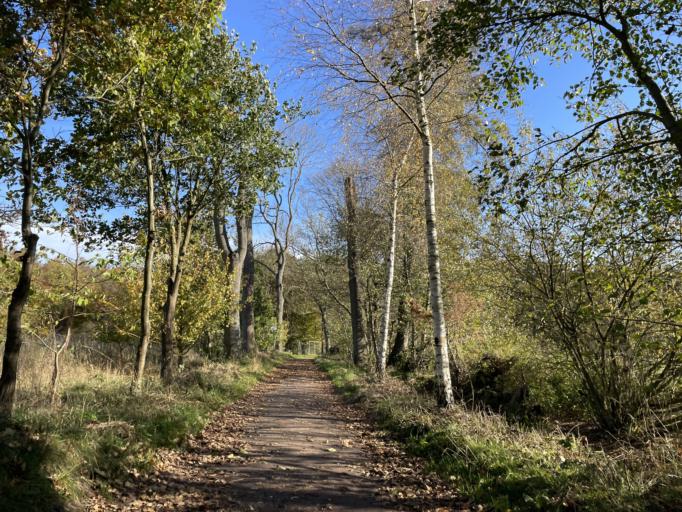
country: DE
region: Lower Saxony
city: Deutsch Evern
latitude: 53.2195
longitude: 10.4208
